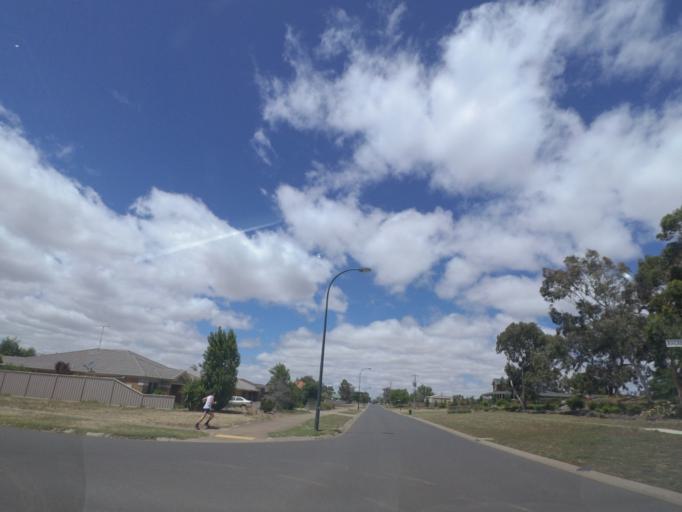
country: AU
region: Victoria
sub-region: Moorabool
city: Bacchus Marsh
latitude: -37.6508
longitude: 144.4436
